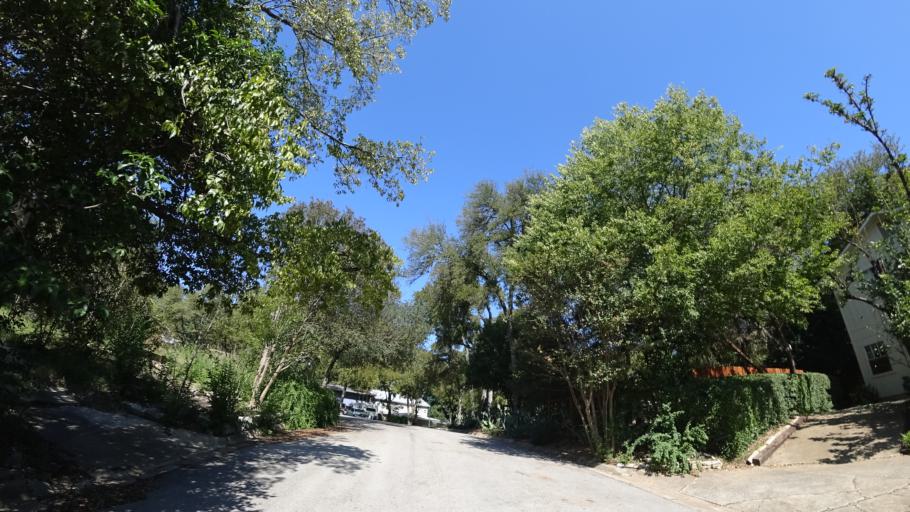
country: US
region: Texas
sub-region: Travis County
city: Rollingwood
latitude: 30.2455
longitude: -97.7867
